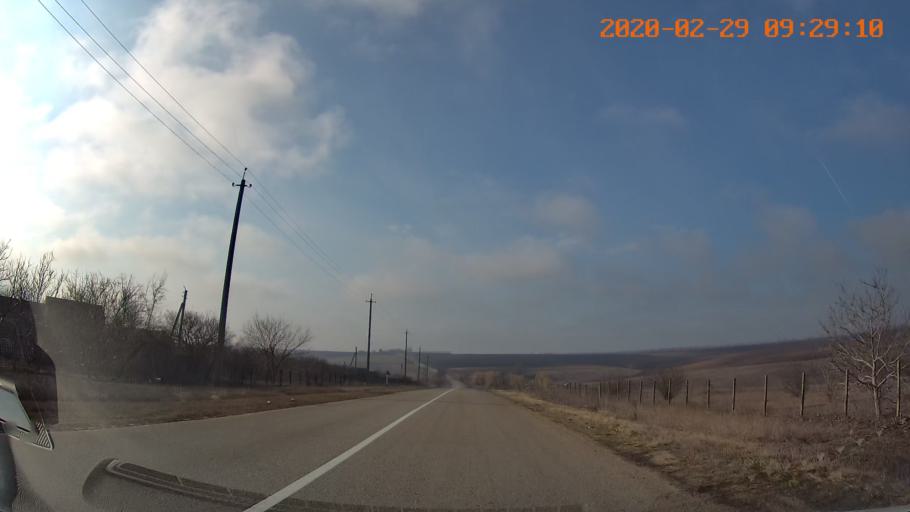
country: UA
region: Odessa
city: Lymanske
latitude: 46.6813
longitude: 29.9234
